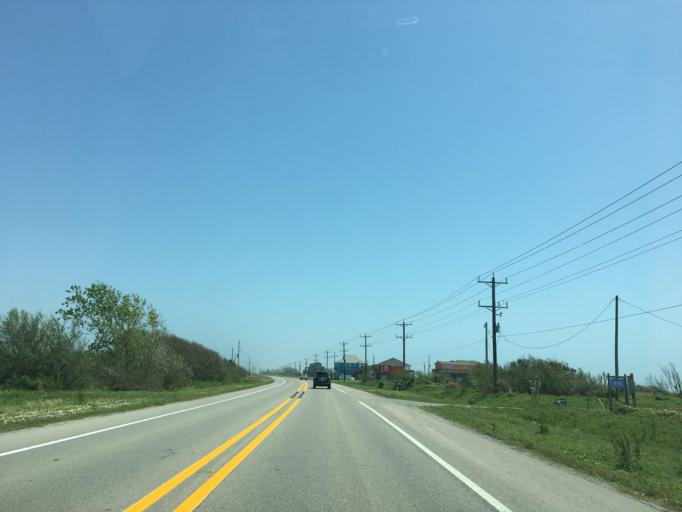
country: US
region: Texas
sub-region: Galveston County
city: Bolivar Peninsula
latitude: 29.4989
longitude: -94.5260
